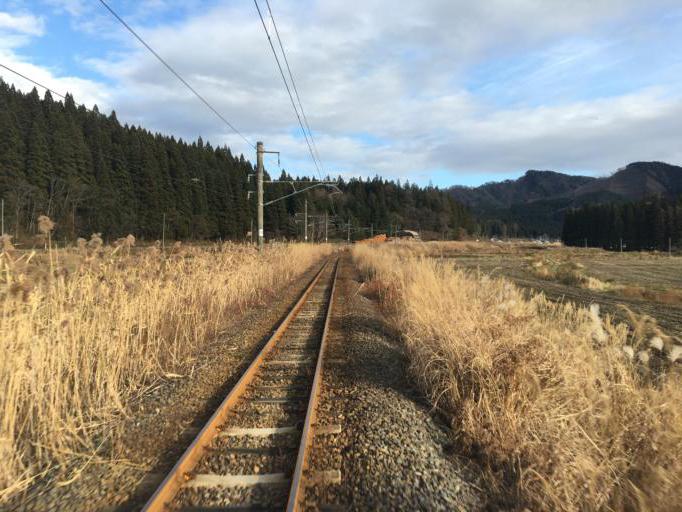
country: JP
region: Yamagata
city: Shinjo
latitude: 38.9742
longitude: 140.3339
